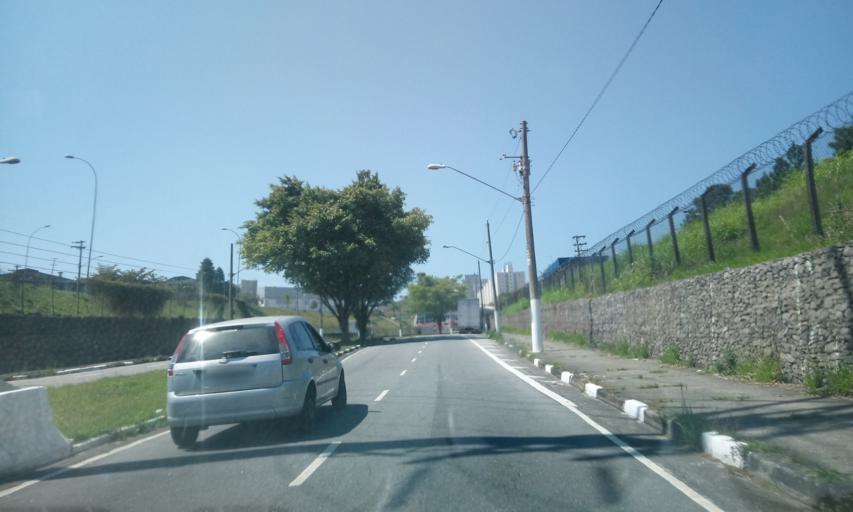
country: BR
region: Sao Paulo
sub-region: Sao Bernardo Do Campo
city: Sao Bernardo do Campo
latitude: -23.6977
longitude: -46.5757
